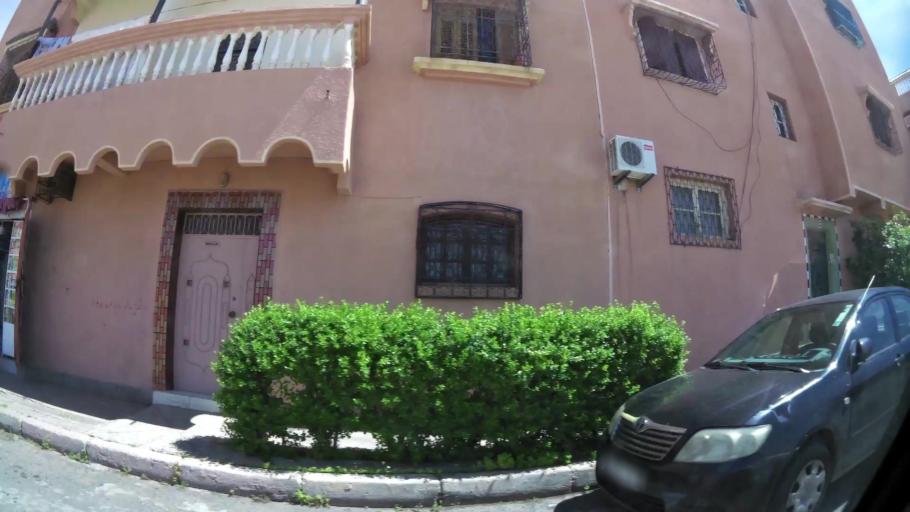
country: MA
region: Marrakech-Tensift-Al Haouz
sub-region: Marrakech
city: Marrakesh
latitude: 31.6583
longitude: -7.9878
